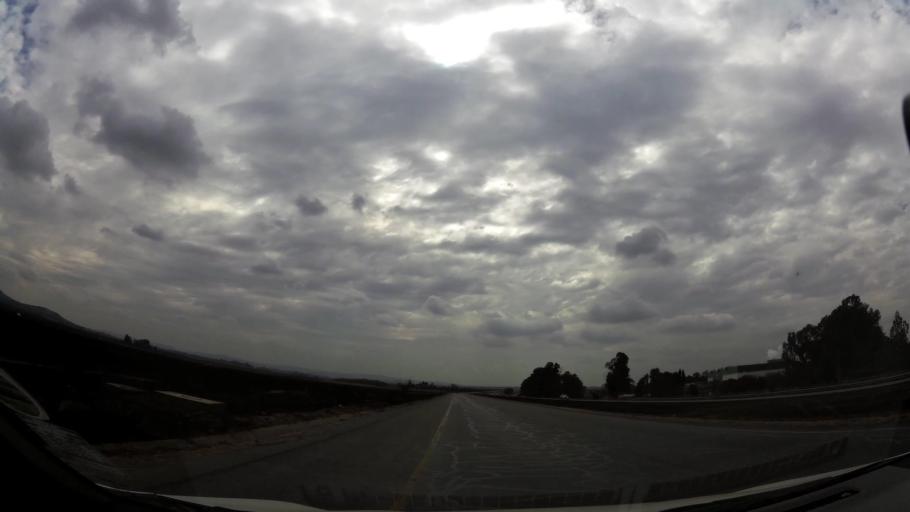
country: ZA
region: Gauteng
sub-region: Sedibeng District Municipality
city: Meyerton
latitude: -26.4088
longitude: 28.0785
